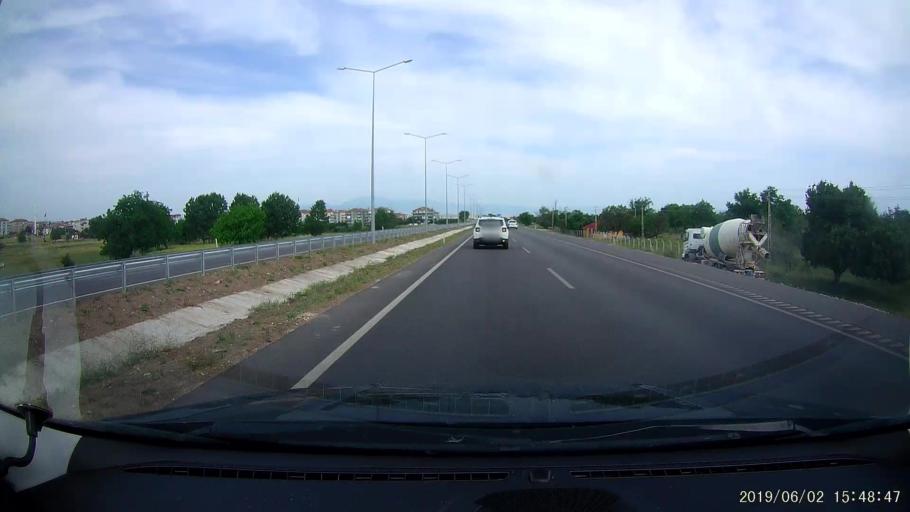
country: TR
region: Amasya
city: Merzifon
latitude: 40.8606
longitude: 35.4484
